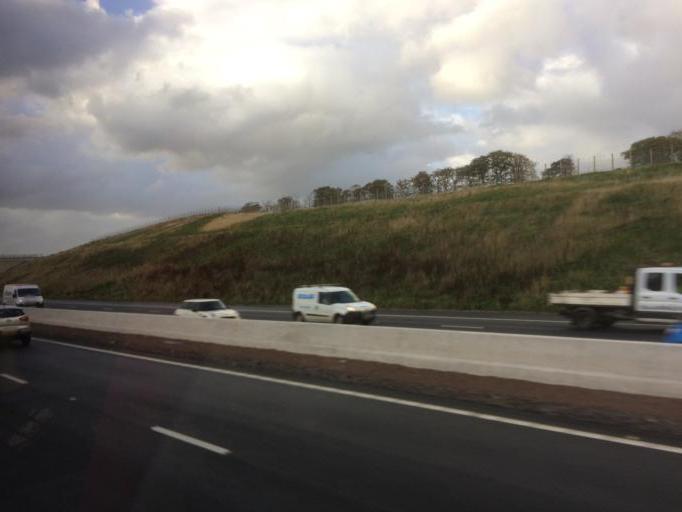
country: GB
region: Scotland
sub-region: North Lanarkshire
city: Coatbridge
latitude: 55.8395
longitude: -4.0371
